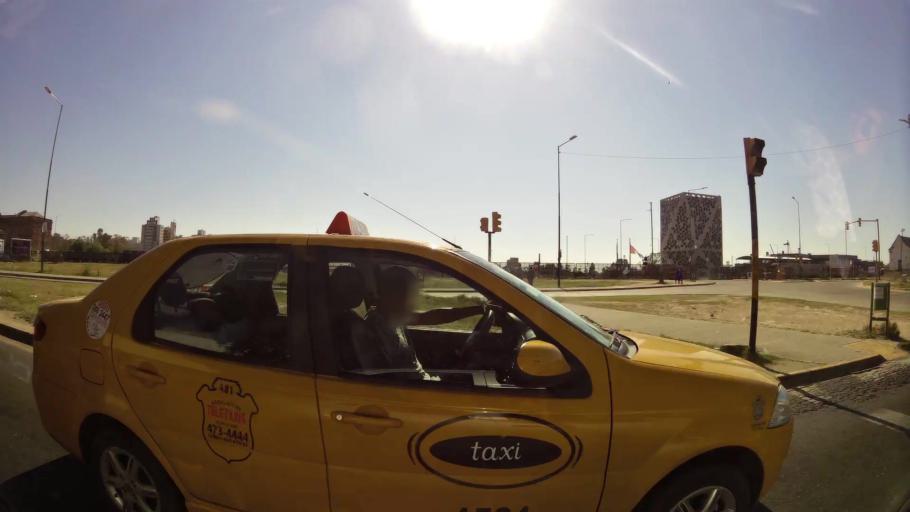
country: AR
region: Cordoba
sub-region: Departamento de Capital
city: Cordoba
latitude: -31.4182
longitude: -64.1761
